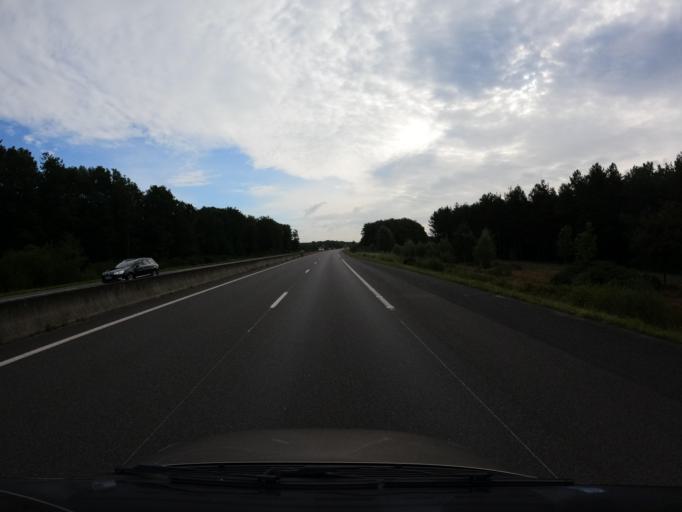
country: FR
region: Centre
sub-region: Departement d'Indre-et-Loire
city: Restigne
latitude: 47.3120
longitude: 0.3098
